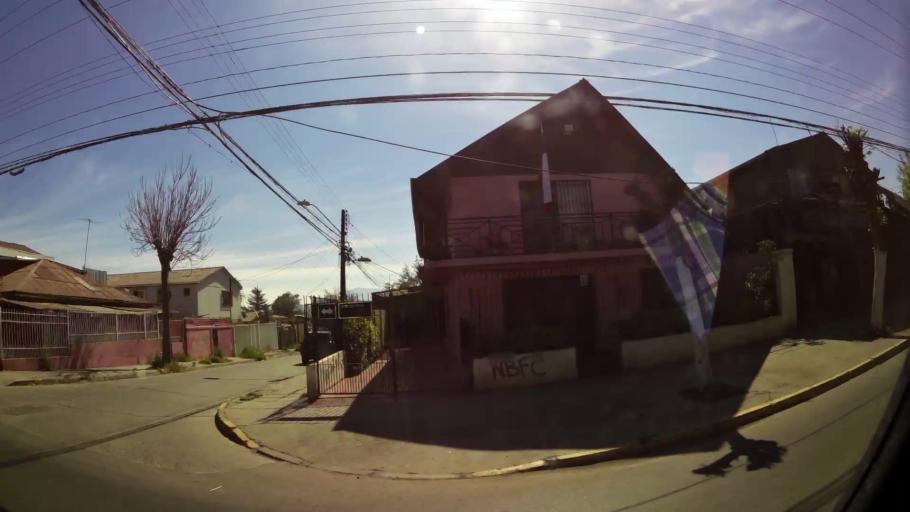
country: CL
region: Santiago Metropolitan
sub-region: Provincia de Santiago
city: Lo Prado
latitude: -33.4982
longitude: -70.7230
